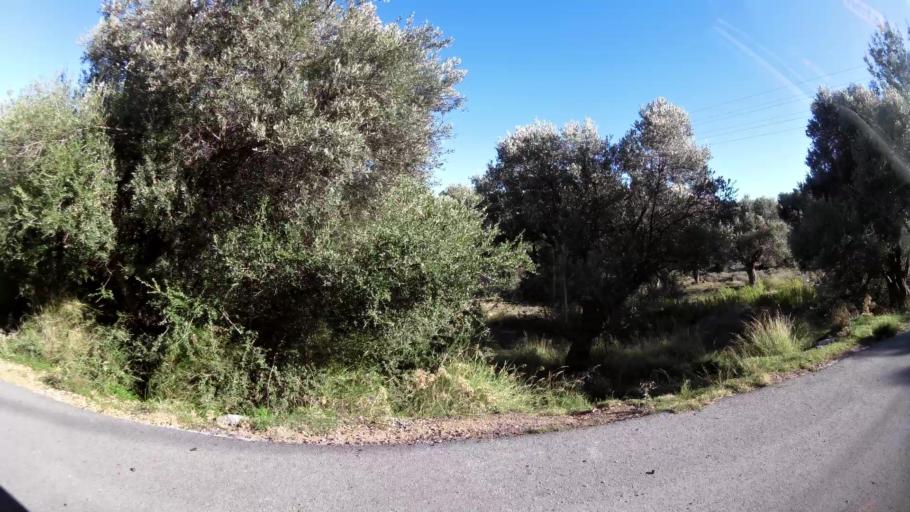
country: GR
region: Attica
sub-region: Nomarchia Anatolikis Attikis
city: Leondarion
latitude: 37.9927
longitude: 23.8420
